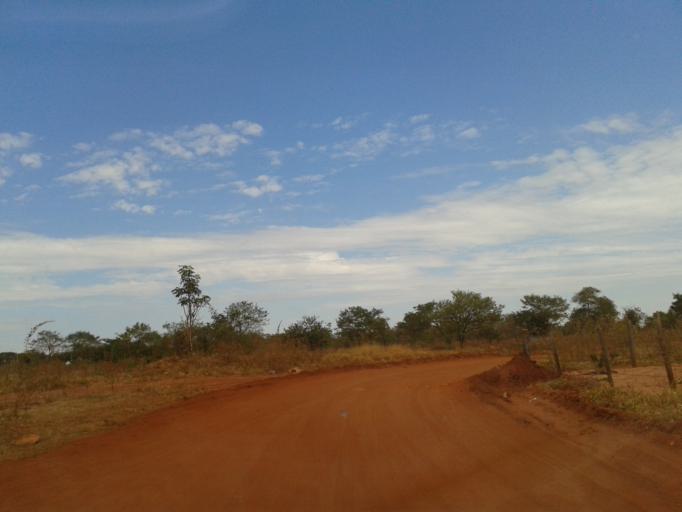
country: BR
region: Minas Gerais
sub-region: Santa Vitoria
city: Santa Vitoria
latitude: -18.8536
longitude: -50.1321
